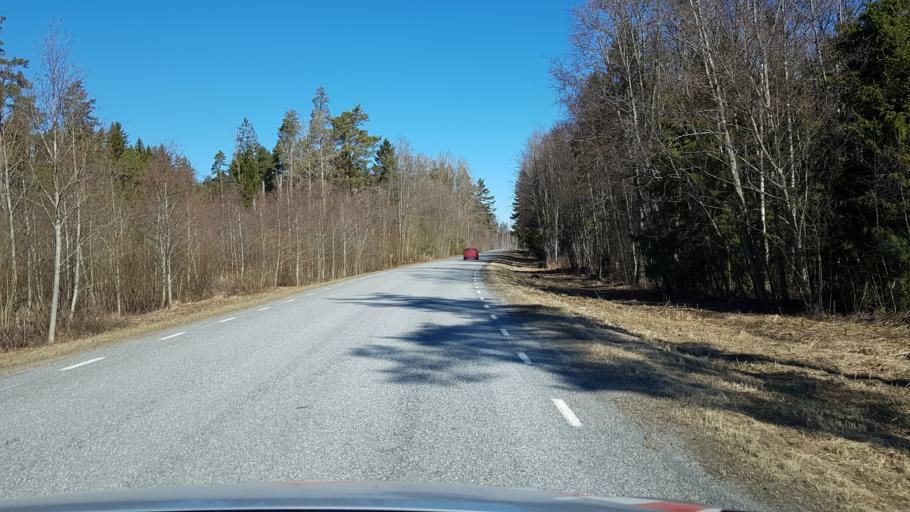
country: EE
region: Laeaene-Virumaa
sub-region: Haljala vald
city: Haljala
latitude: 59.4803
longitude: 26.2478
